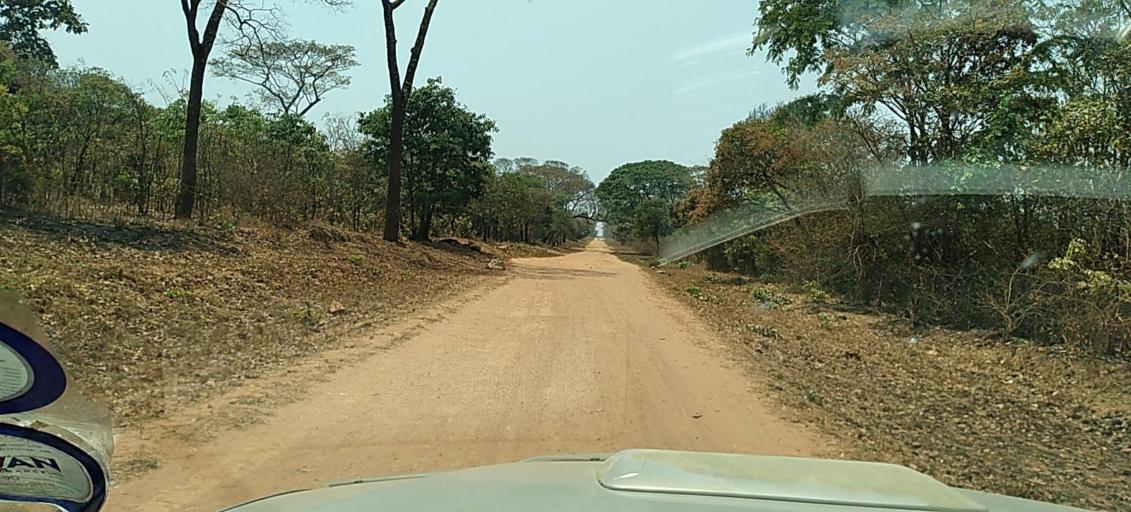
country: ZM
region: North-Western
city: Kasempa
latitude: -13.5502
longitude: 26.0284
